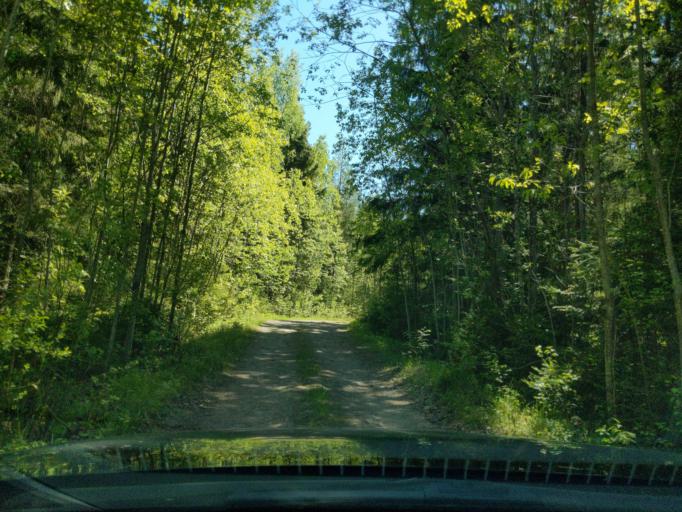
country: FI
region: Paijanne Tavastia
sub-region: Lahti
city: Lahti
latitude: 61.0518
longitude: 25.6974
